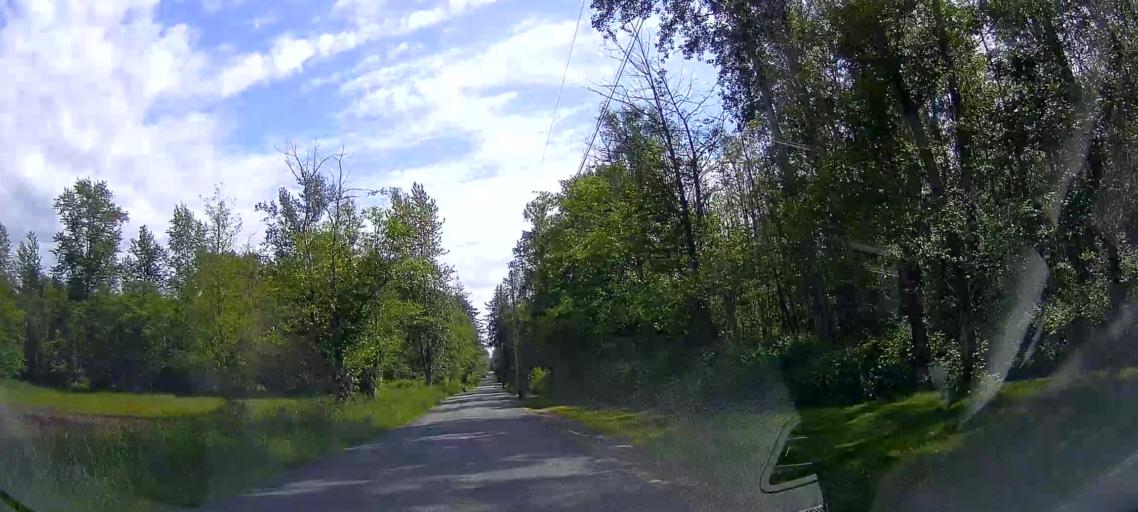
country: US
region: Washington
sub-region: Skagit County
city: Burlington
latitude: 48.5434
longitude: -122.3621
